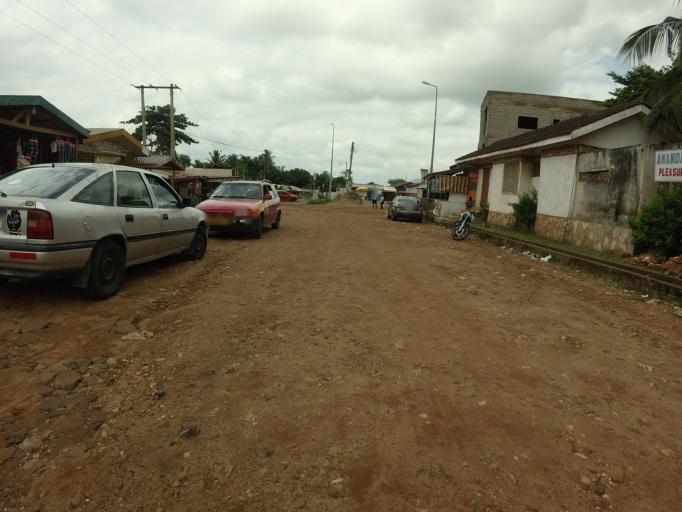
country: GH
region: Volta
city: Ho
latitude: 6.5935
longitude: 0.4705
